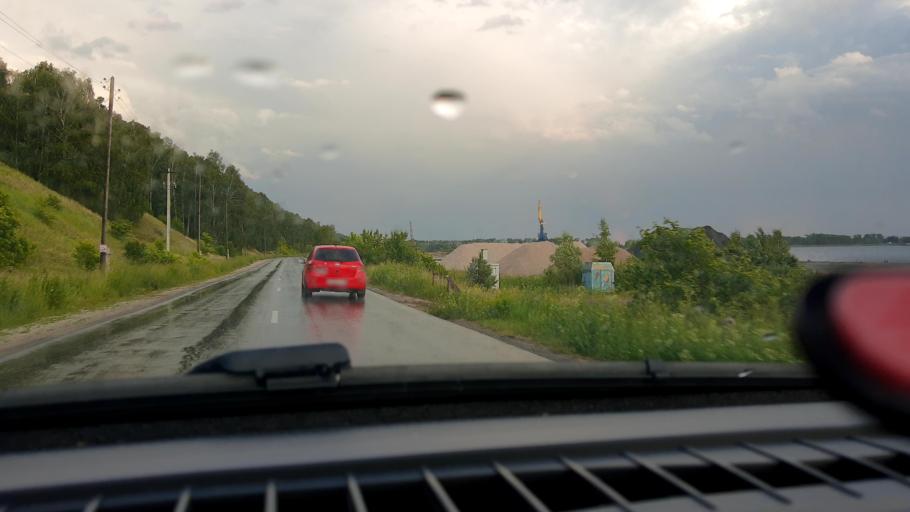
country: RU
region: Nizjnij Novgorod
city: Gorodets
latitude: 56.6770
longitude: 43.4417
